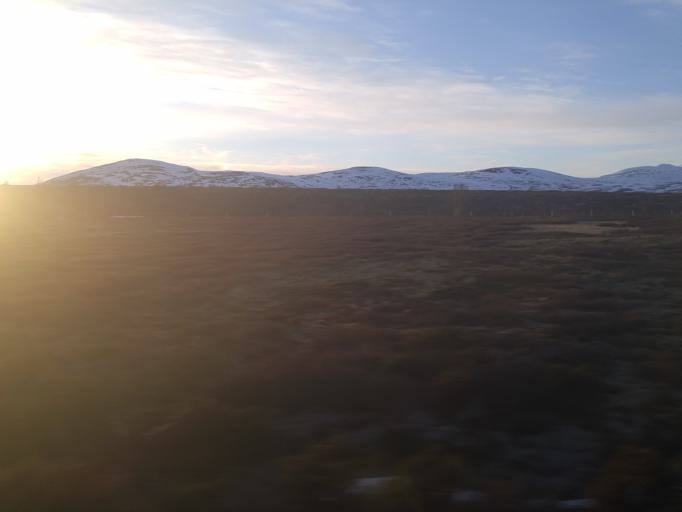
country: NO
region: Oppland
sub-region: Dovre
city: Dovre
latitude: 62.1074
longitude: 9.2542
